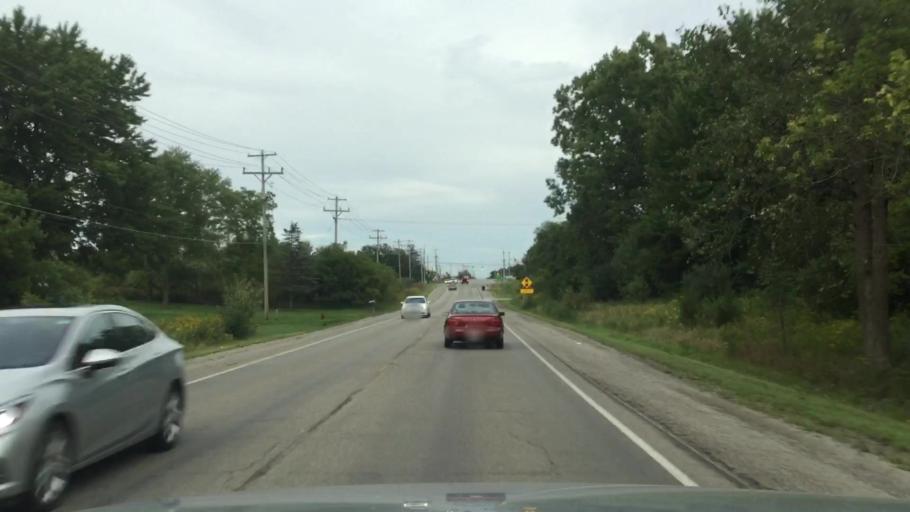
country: US
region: Michigan
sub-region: Genesee County
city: Grand Blanc
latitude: 42.8868
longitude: -83.6346
